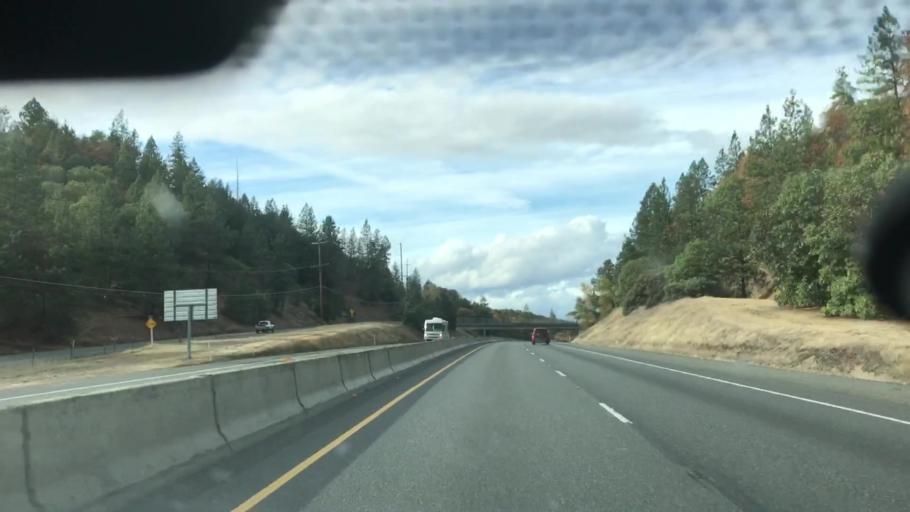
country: US
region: Oregon
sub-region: Josephine County
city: Grants Pass
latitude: 42.4763
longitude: -123.3490
